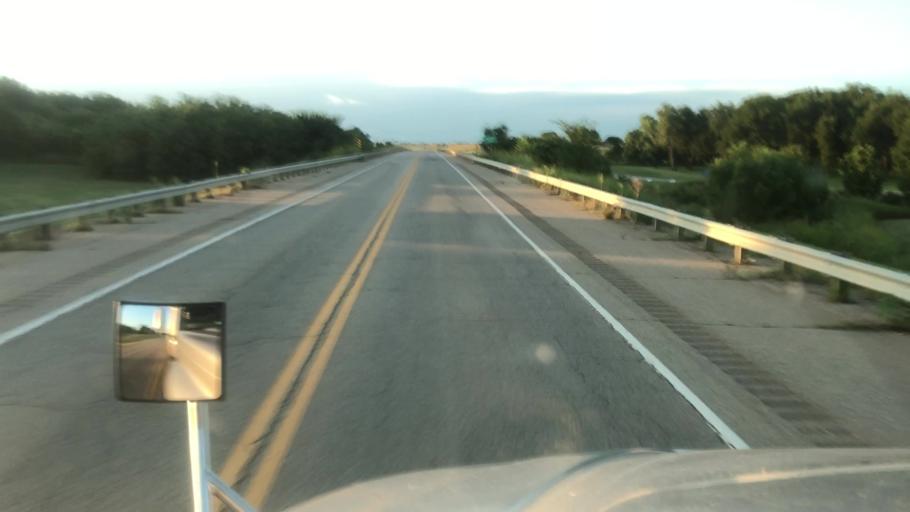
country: US
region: Oklahoma
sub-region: Osage County
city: McCord
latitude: 36.4933
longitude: -97.0736
